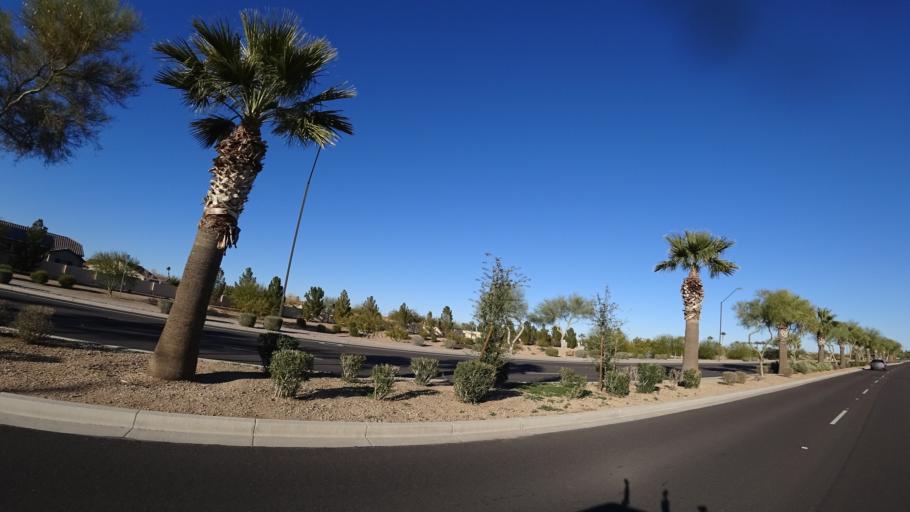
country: US
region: Arizona
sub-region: Maricopa County
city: Litchfield Park
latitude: 33.4647
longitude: -112.4130
